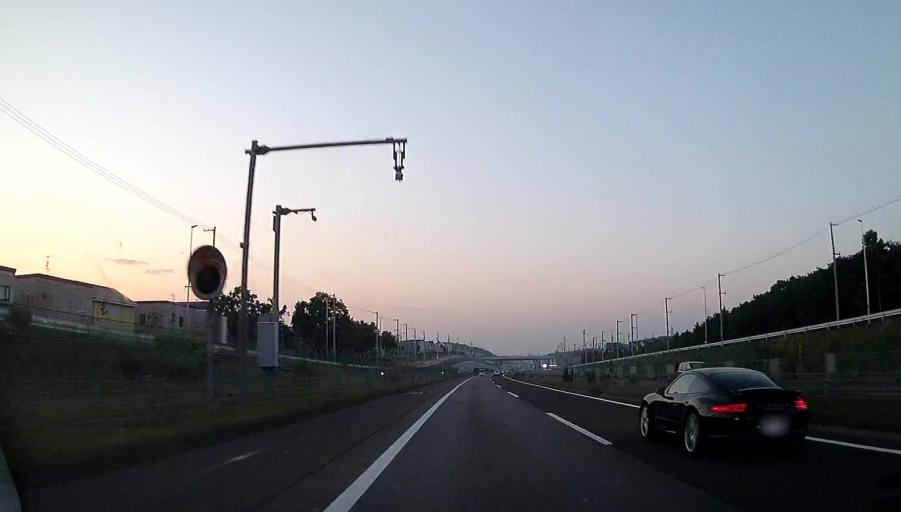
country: JP
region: Hokkaido
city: Kitahiroshima
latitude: 42.9877
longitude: 141.4703
